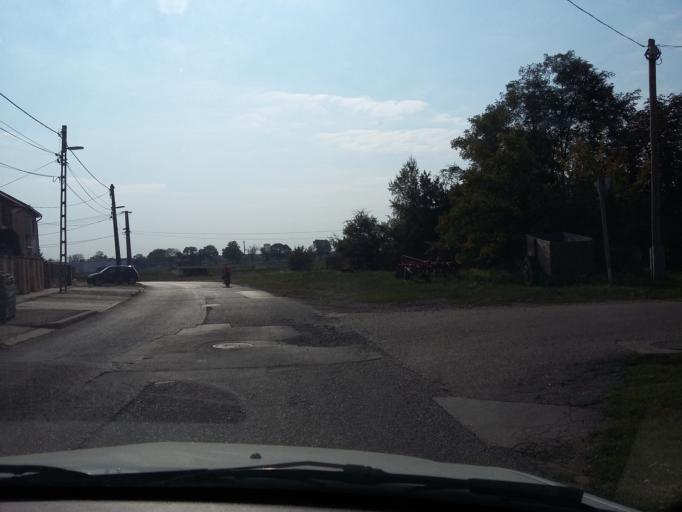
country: HU
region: Borsod-Abauj-Zemplen
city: Bekecs
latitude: 48.1551
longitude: 21.1870
